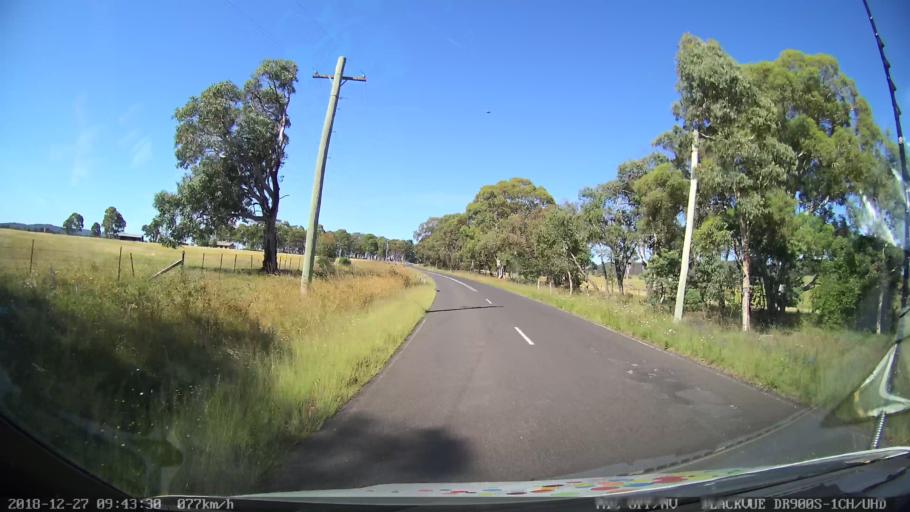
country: AU
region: New South Wales
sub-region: Lithgow
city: Portland
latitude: -33.3067
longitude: 150.0005
